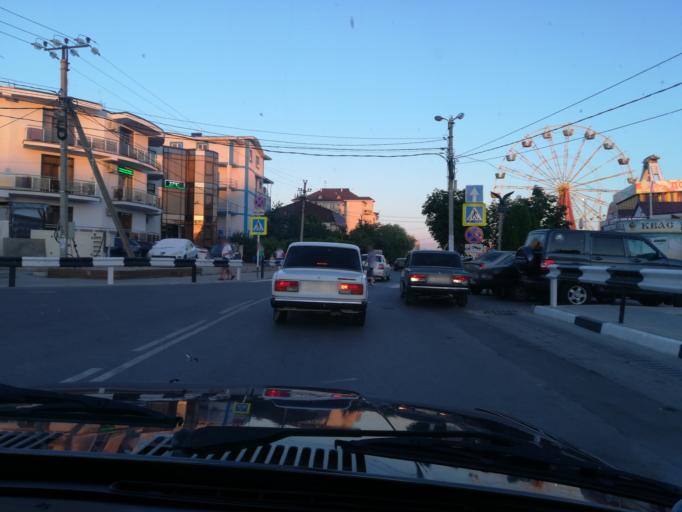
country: RU
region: Krasnodarskiy
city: Vityazevo
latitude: 44.9883
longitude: 37.2567
